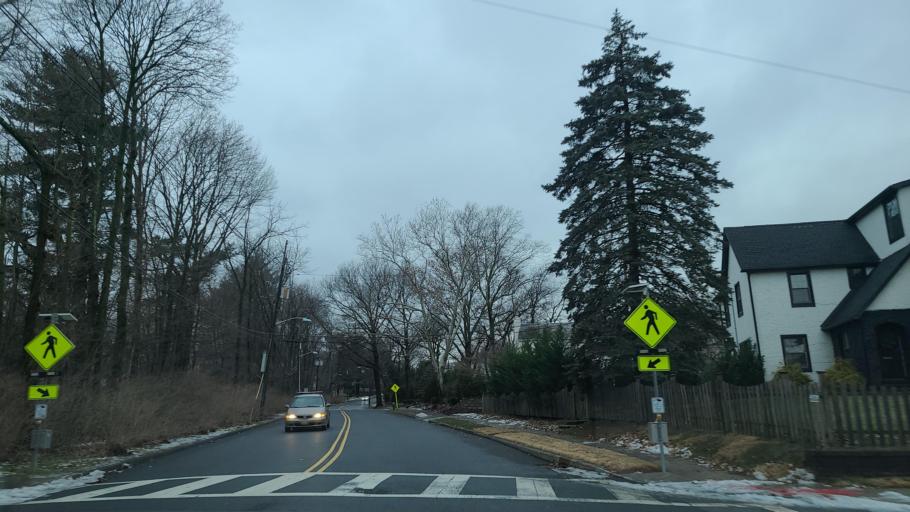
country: US
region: New Jersey
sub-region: Essex County
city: Brookdale
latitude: 40.8381
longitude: -74.1899
